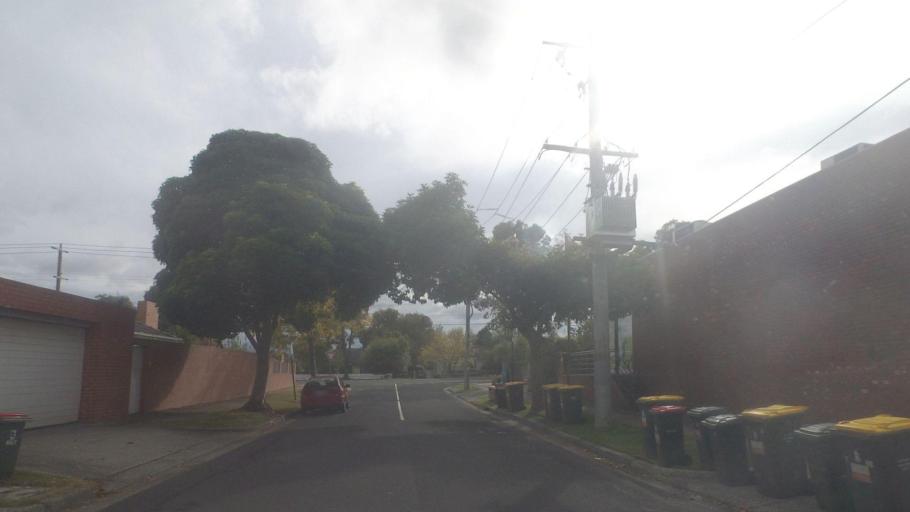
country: AU
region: Victoria
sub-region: Whitehorse
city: Blackburn South
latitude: -37.8320
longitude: 145.1453
